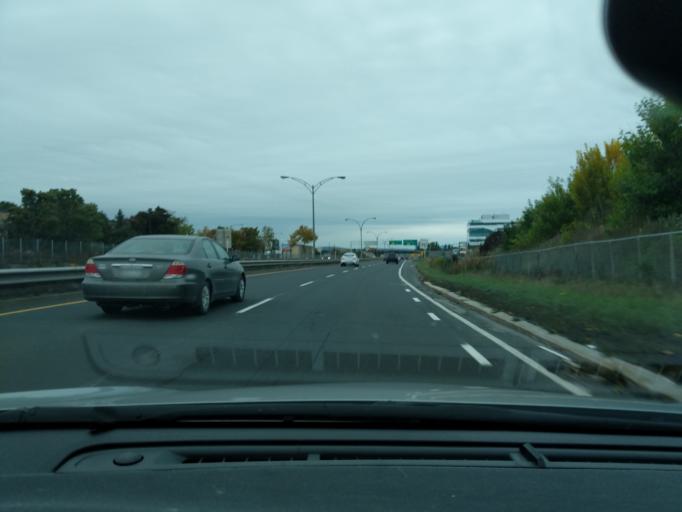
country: CA
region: Quebec
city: L'Ancienne-Lorette
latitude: 46.7626
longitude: -71.3091
